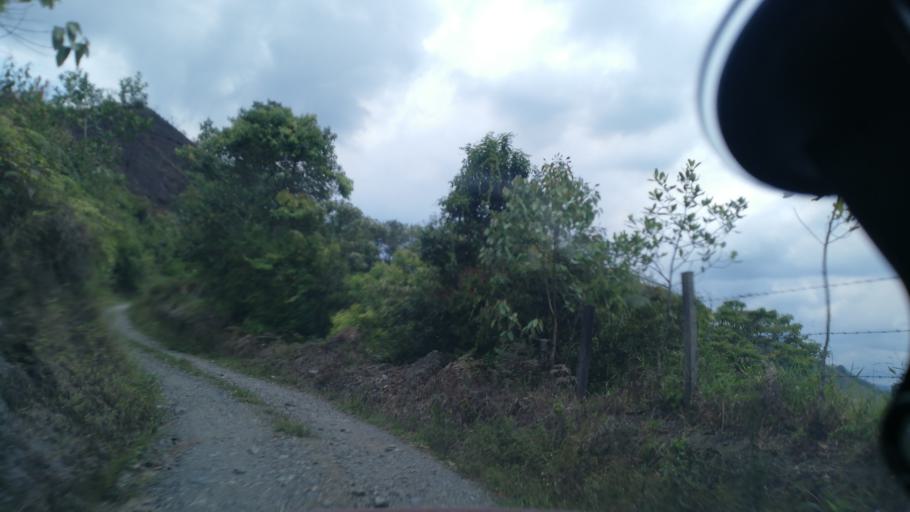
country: CO
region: Cundinamarca
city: Vergara
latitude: 5.2029
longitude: -74.2782
